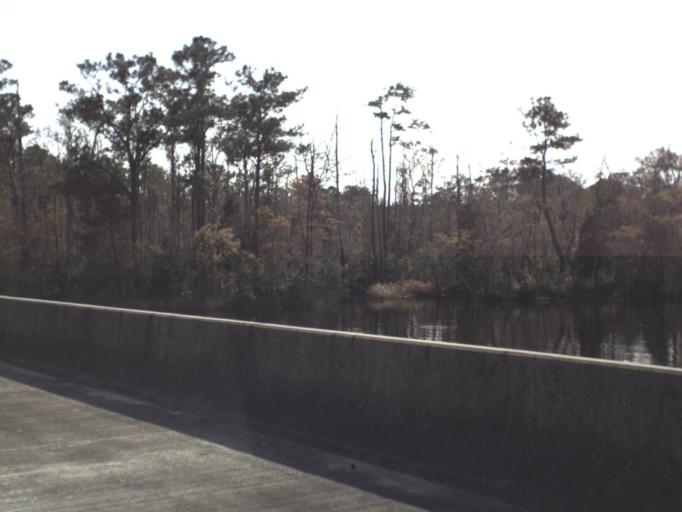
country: US
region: Florida
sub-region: Franklin County
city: Carrabelle
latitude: 29.9878
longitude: -84.5022
